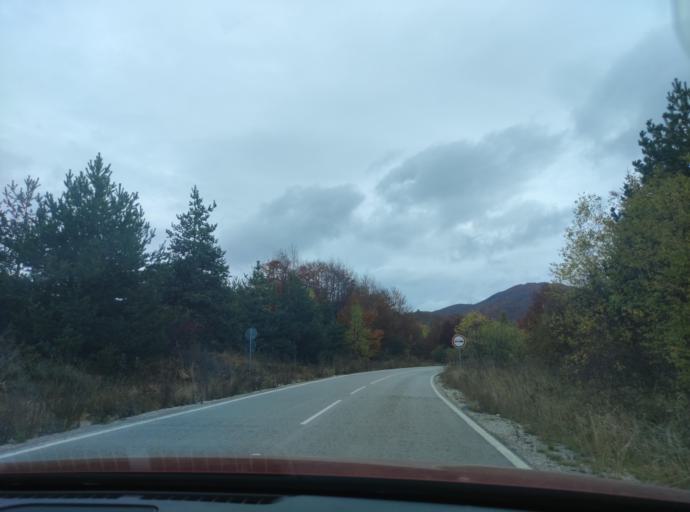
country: BG
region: Sofiya
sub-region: Obshtina Godech
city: Godech
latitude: 43.1039
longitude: 23.1027
